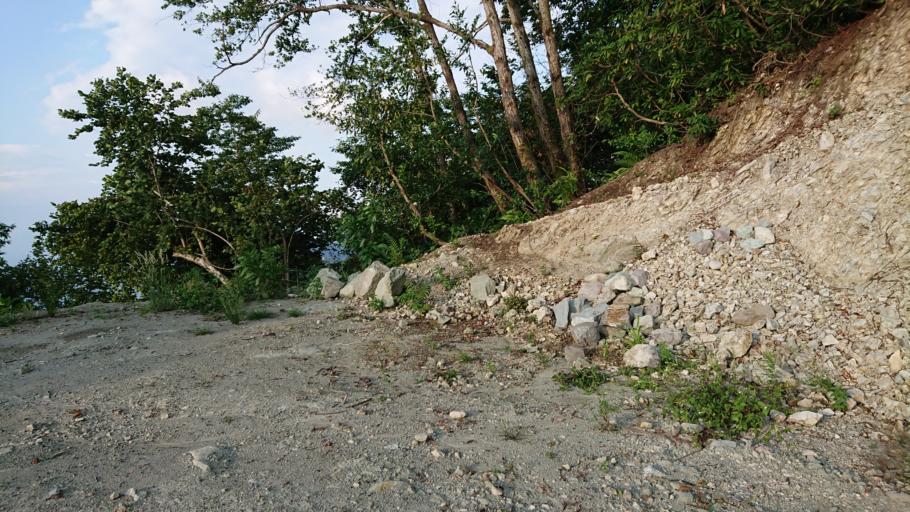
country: TR
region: Rize
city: Rize
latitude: 40.9904
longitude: 40.5050
